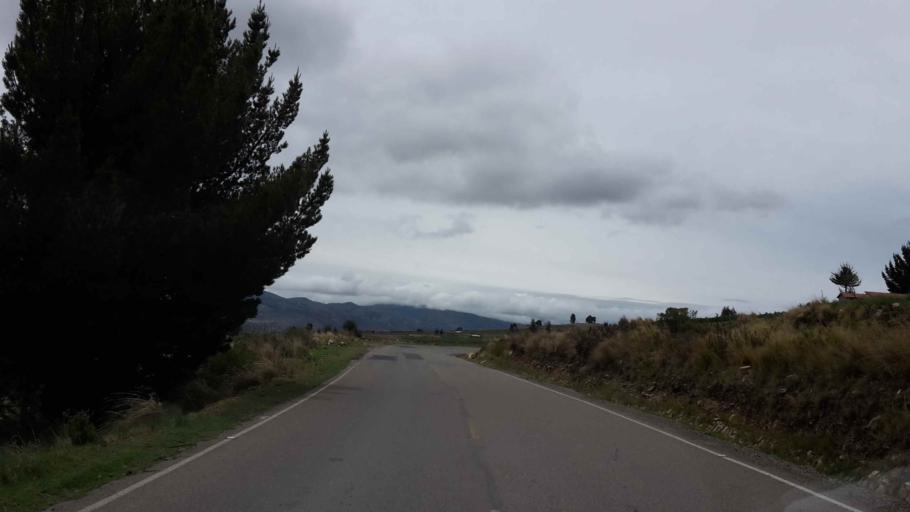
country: BO
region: Cochabamba
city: Arani
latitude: -17.4720
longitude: -65.6507
